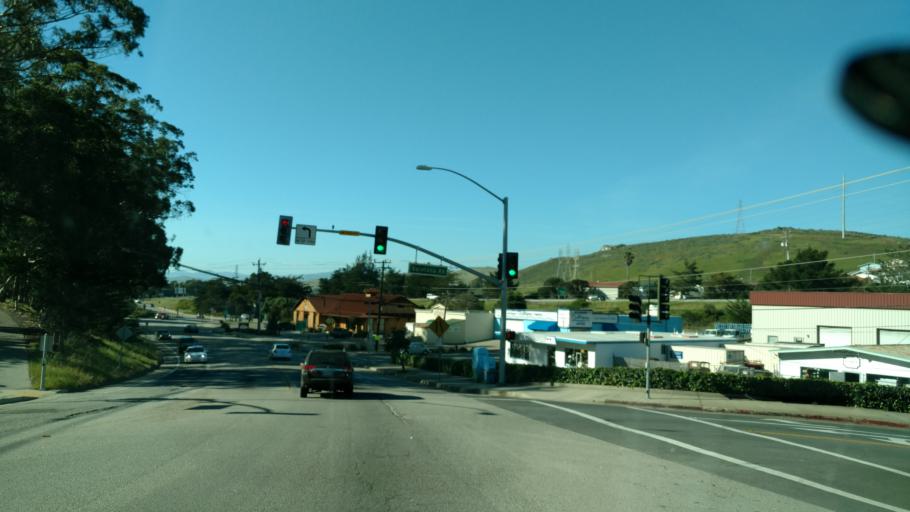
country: US
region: California
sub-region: San Luis Obispo County
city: Morro Bay
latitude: 35.3712
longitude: -120.8501
